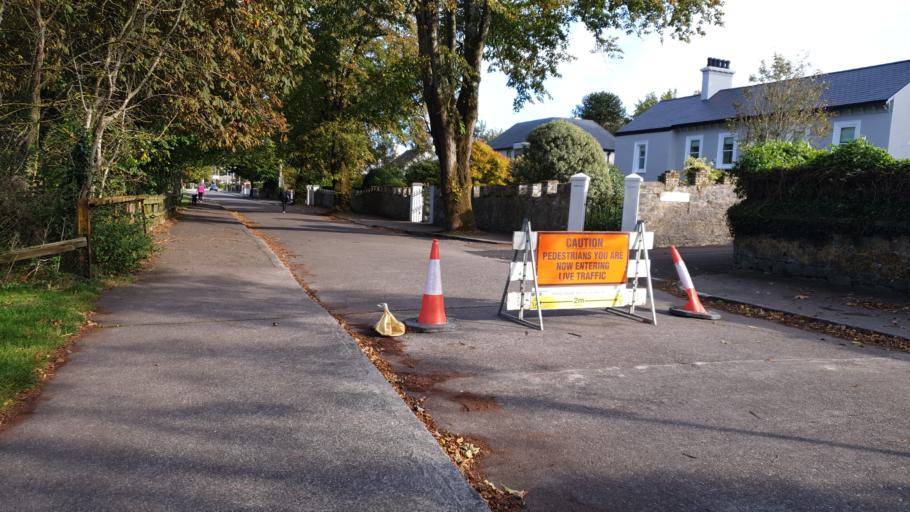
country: IE
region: Munster
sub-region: County Cork
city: Cork
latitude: 51.8984
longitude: -8.4171
